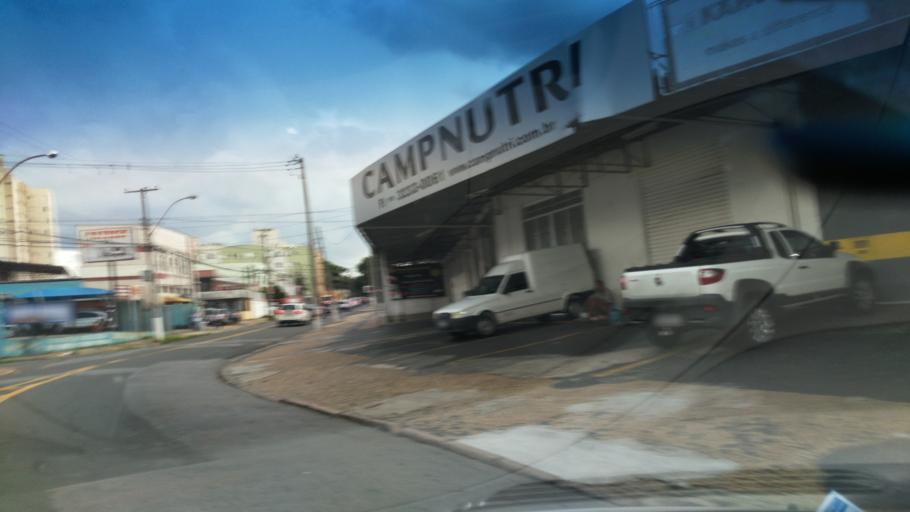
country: BR
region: Sao Paulo
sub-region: Campinas
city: Campinas
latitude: -22.9165
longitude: -47.0570
